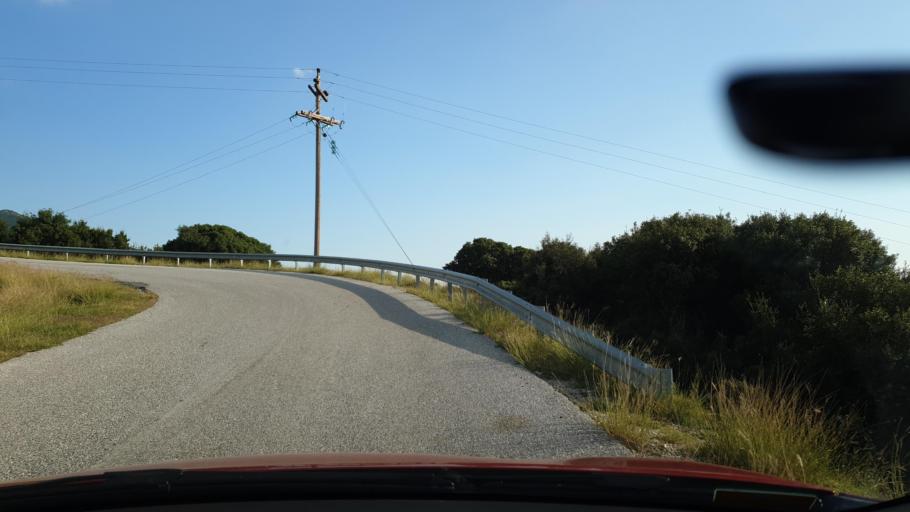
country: GR
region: Central Macedonia
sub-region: Nomos Thessalonikis
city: Peristera
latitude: 40.5251
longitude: 23.1906
